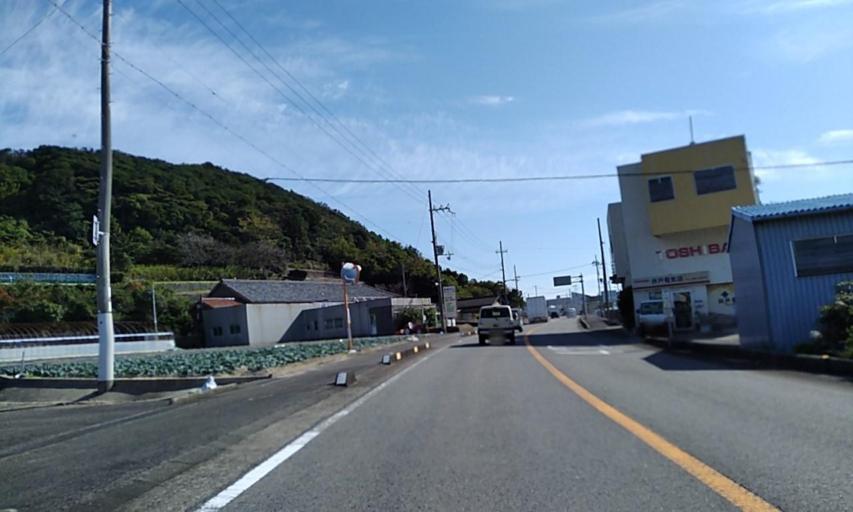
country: JP
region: Wakayama
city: Gobo
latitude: 33.8362
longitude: 135.1783
